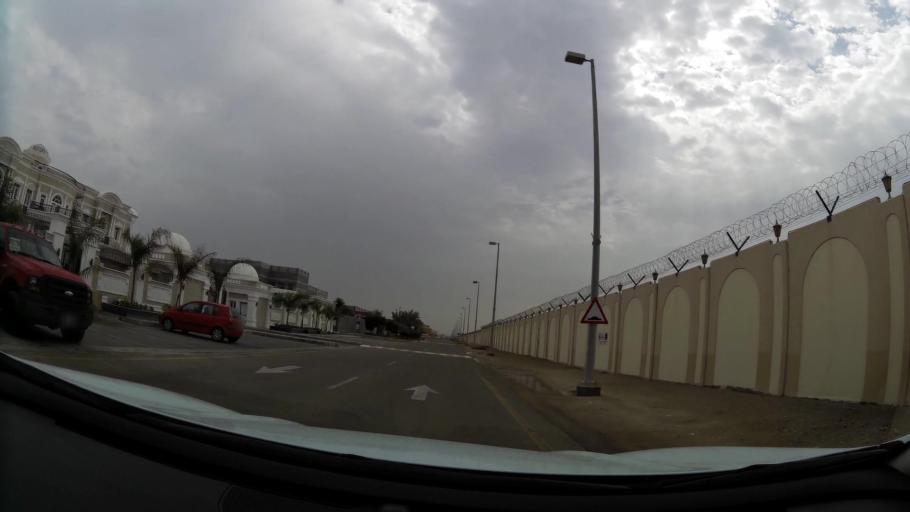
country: AE
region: Abu Dhabi
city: Abu Dhabi
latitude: 24.4378
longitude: 54.4476
